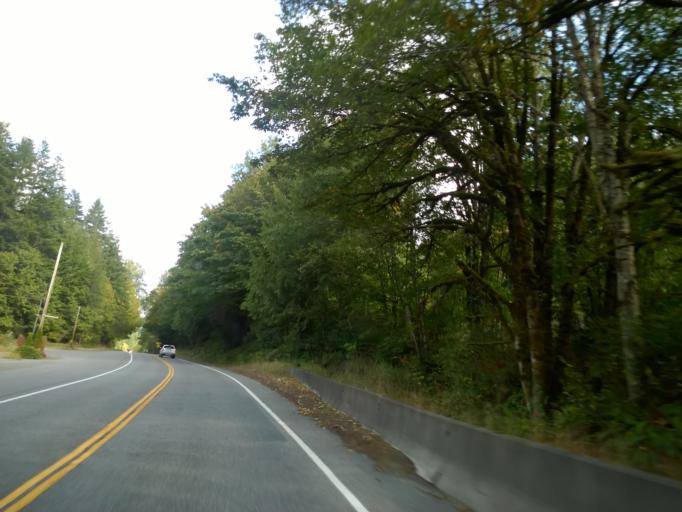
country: US
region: Washington
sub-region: Snohomish County
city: Gold Bar
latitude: 47.7119
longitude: -121.3255
